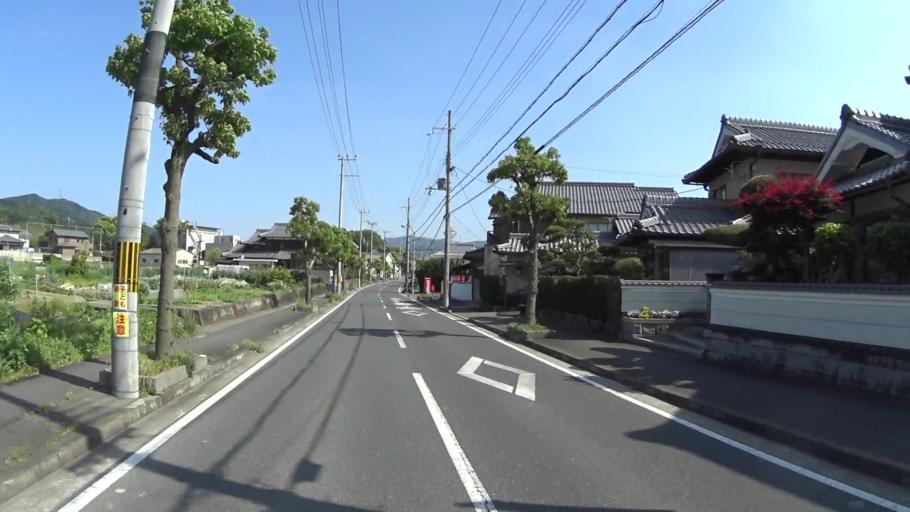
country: JP
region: Kyoto
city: Kameoka
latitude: 35.0246
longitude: 135.5879
